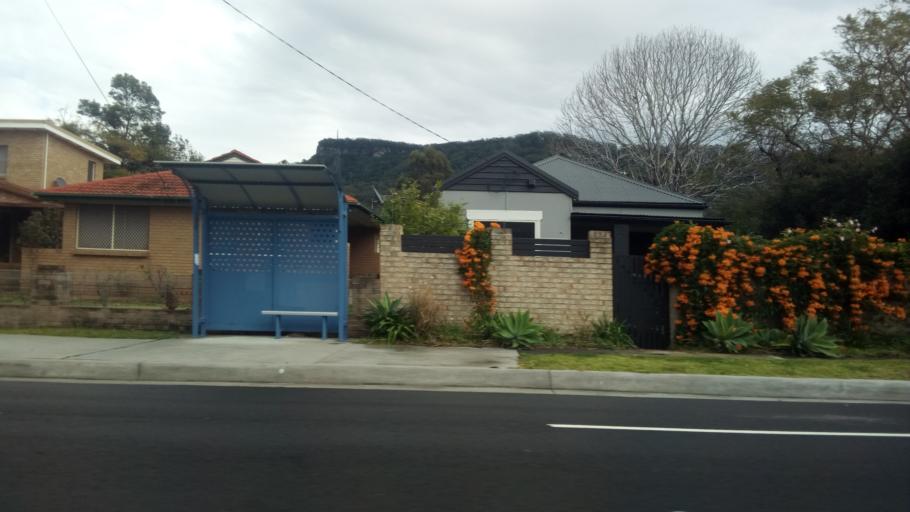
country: AU
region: New South Wales
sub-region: Wollongong
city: Corrimal
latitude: -34.3655
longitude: 150.8986
